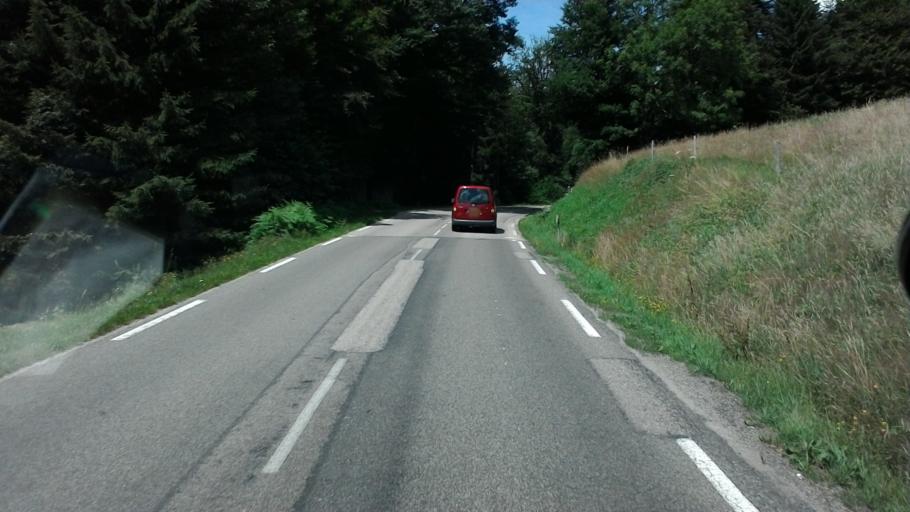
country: FR
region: Lorraine
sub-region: Departement des Vosges
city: Le Tholy
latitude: 48.0918
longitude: 6.7297
